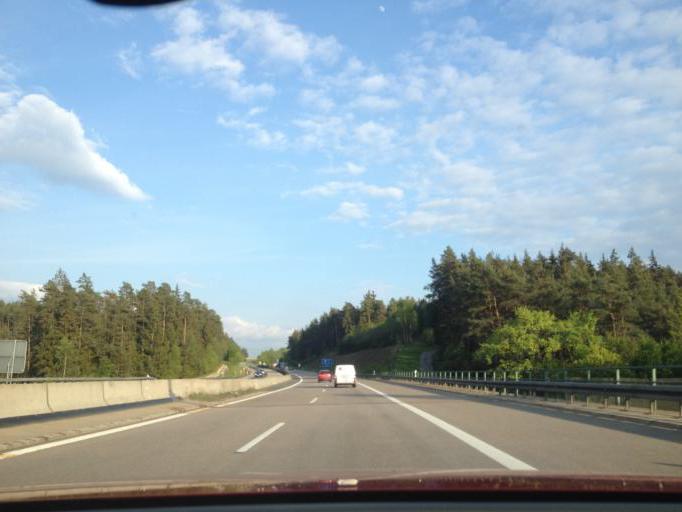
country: DE
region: Bavaria
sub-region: Upper Palatinate
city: Windischeschenbach
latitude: 49.8178
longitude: 12.1690
